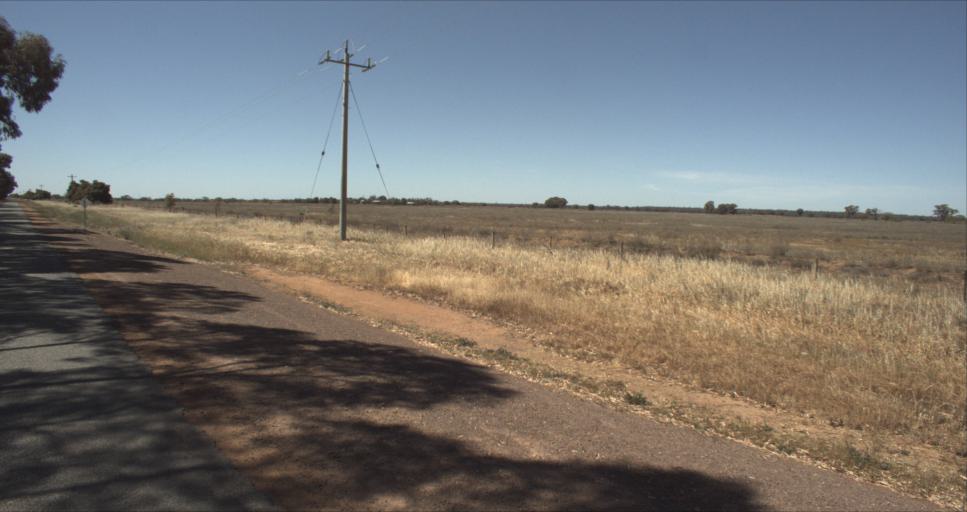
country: AU
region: New South Wales
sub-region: Leeton
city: Leeton
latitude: -34.5777
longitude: 146.2629
